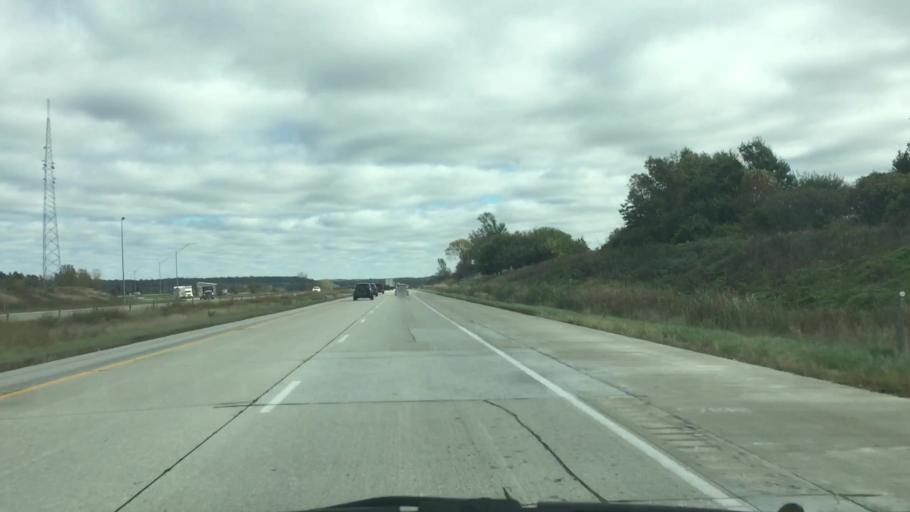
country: US
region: Iowa
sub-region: Polk County
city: Mitchellville
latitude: 41.6805
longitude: -93.3425
